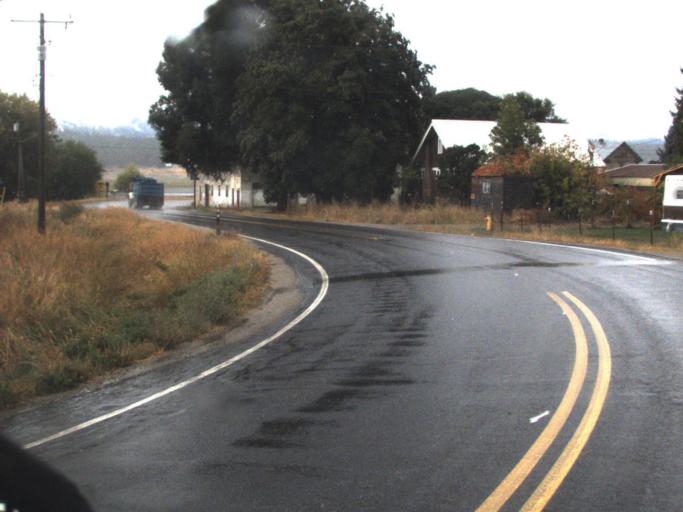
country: US
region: Washington
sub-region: Stevens County
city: Chewelah
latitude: 48.1762
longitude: -117.7252
